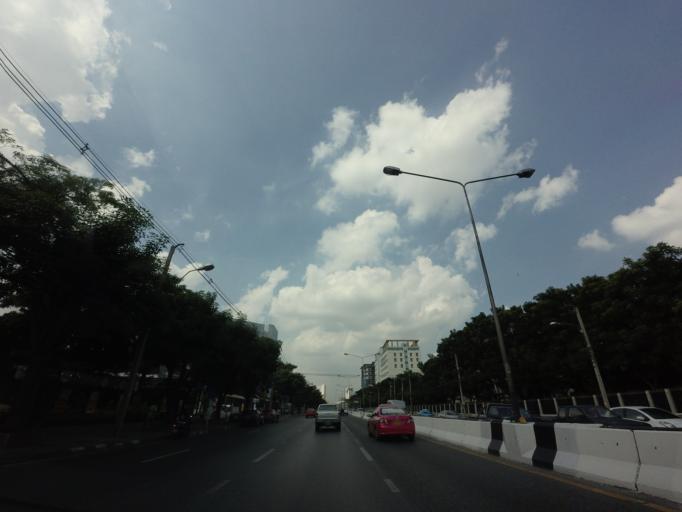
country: TH
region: Bangkok
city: Chatuchak
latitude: 13.8426
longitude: 100.5704
